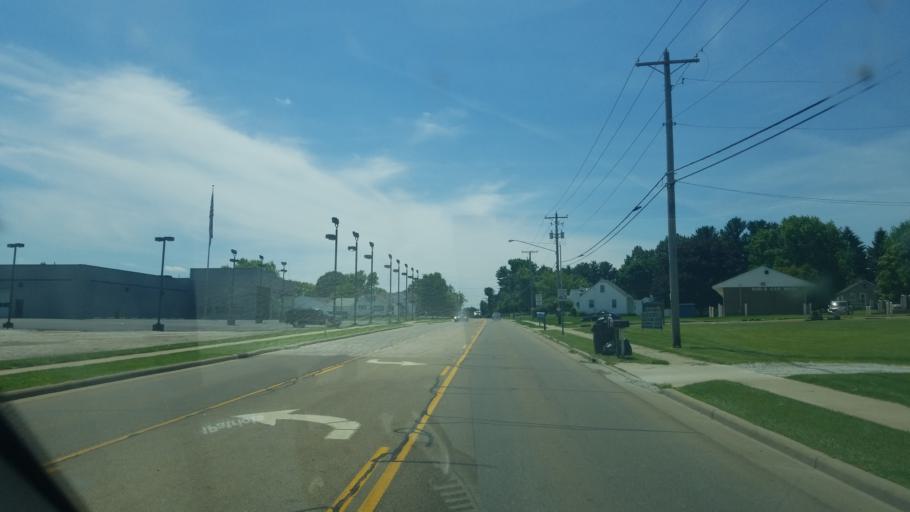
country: US
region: Ohio
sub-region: Stark County
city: Louisville
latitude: 40.8348
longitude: -81.2802
